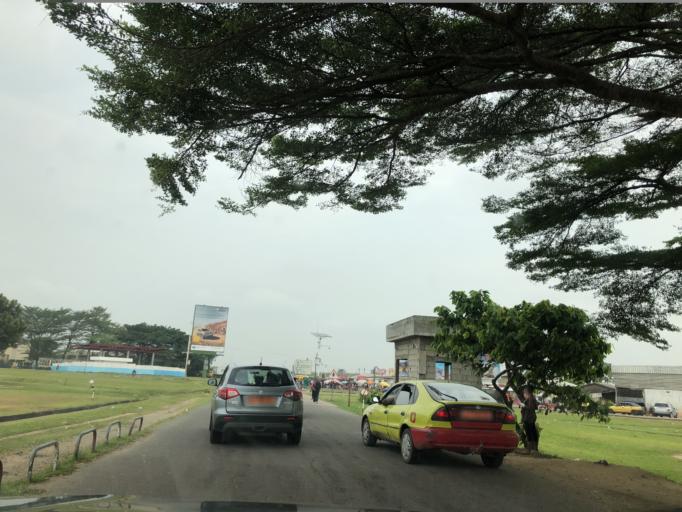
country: CM
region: Littoral
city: Douala
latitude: 4.0142
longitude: 9.7185
